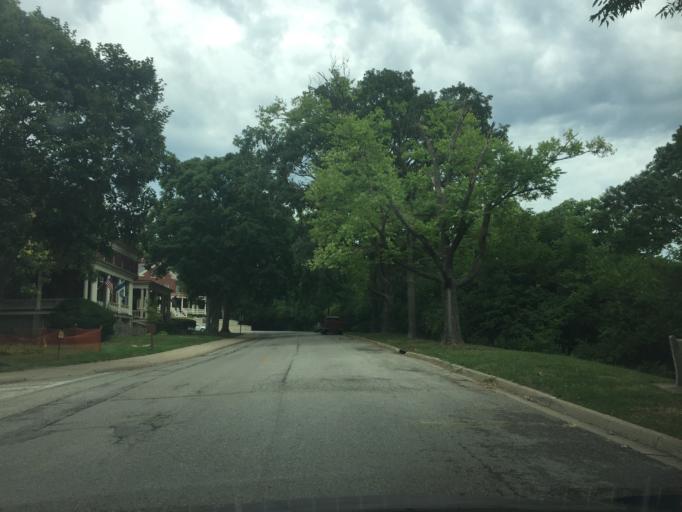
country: US
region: Kansas
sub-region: Leavenworth County
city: Leavenworth
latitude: 39.3496
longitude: -94.9129
